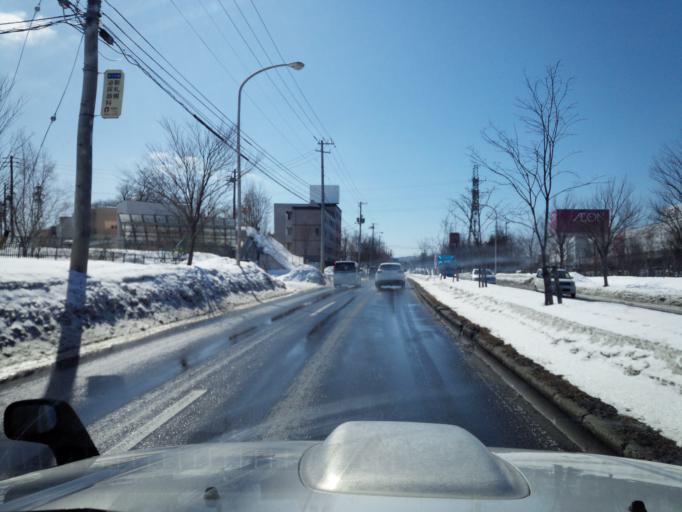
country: JP
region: Hokkaido
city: Kitahiroshima
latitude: 42.9971
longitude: 141.4603
